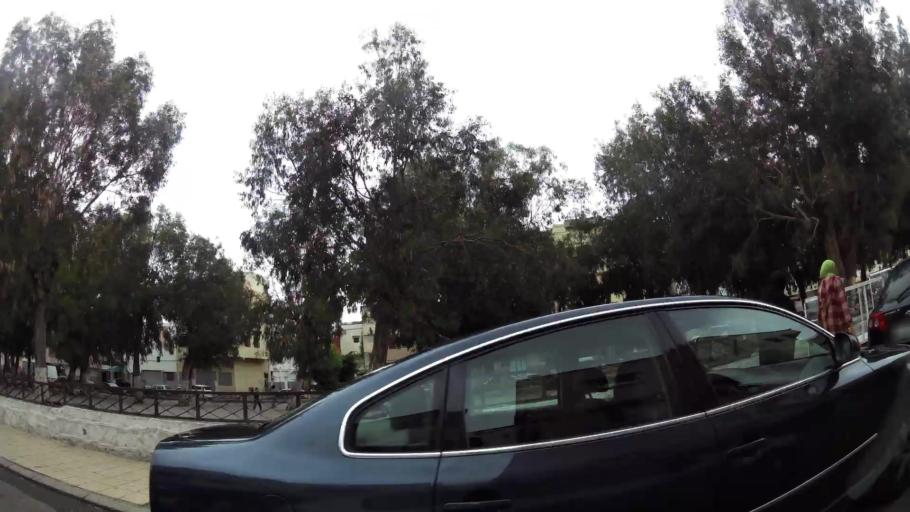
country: MA
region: Rabat-Sale-Zemmour-Zaer
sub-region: Rabat
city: Rabat
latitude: 33.9841
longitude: -6.8212
